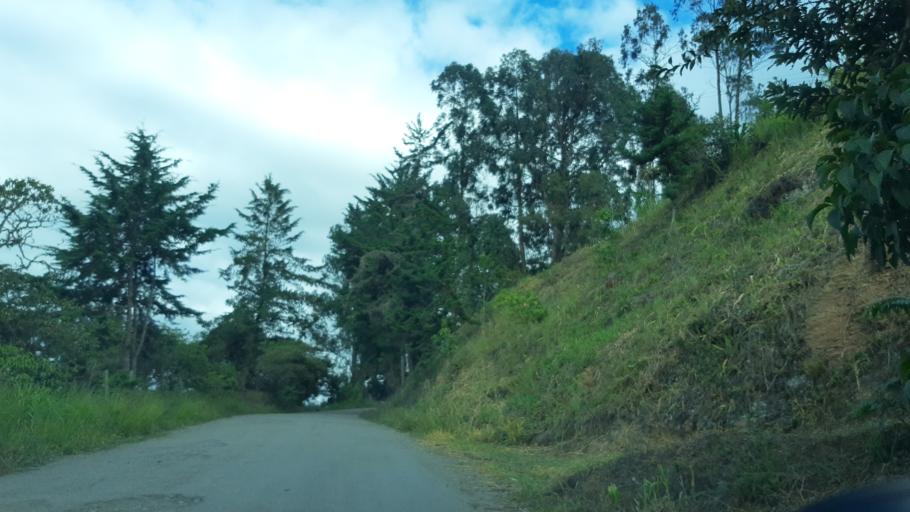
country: CO
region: Cundinamarca
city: Tenza
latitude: 5.0467
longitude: -73.4179
